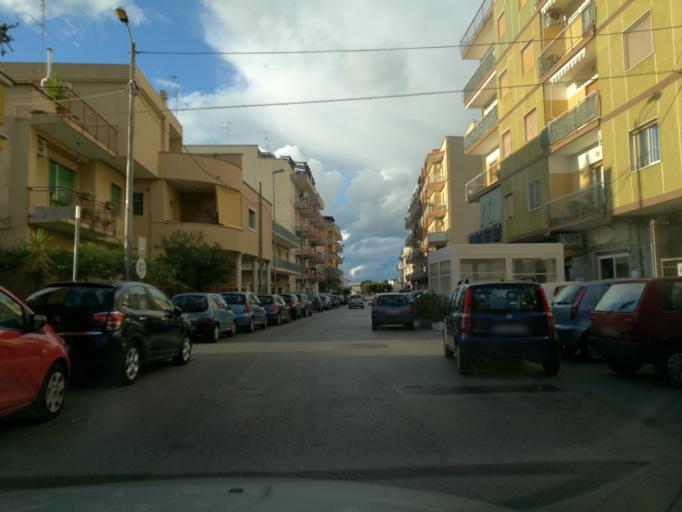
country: IT
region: Apulia
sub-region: Provincia di Bari
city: Valenzano
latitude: 41.0455
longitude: 16.8856
